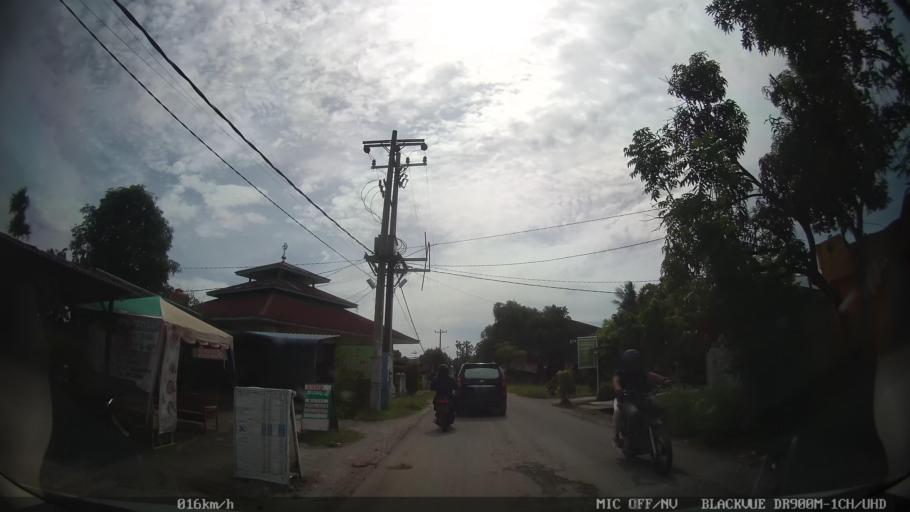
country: ID
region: North Sumatra
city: Percut
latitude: 3.6198
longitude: 98.7950
